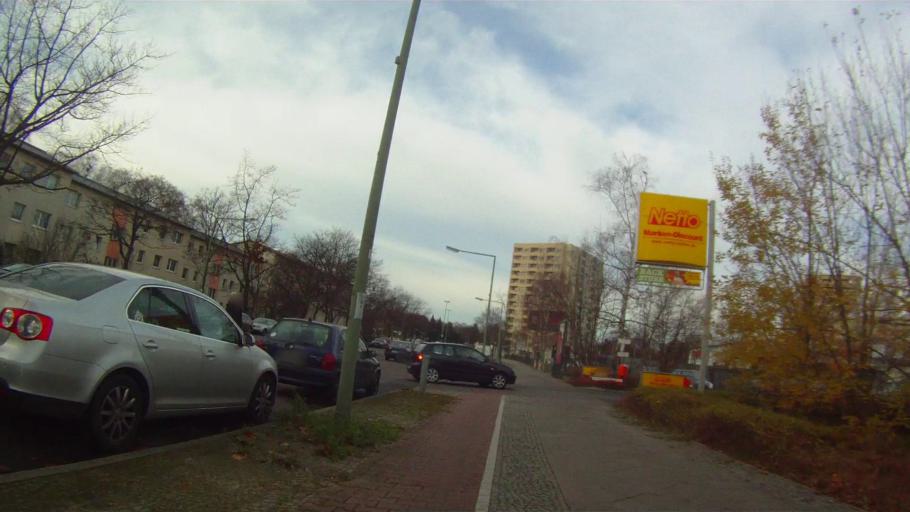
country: DE
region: Berlin
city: Buckow
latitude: 52.4259
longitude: 13.4484
